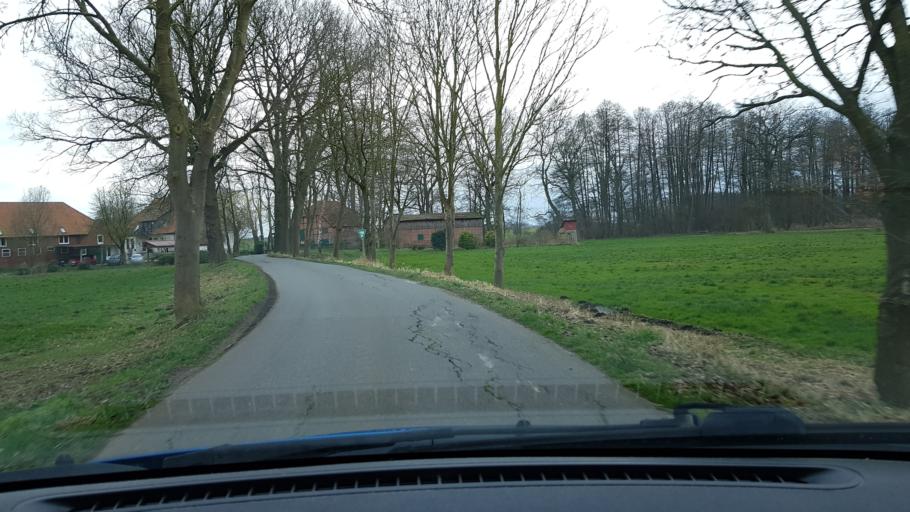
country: DE
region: Lower Saxony
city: Oetzen
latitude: 53.0166
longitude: 10.6573
